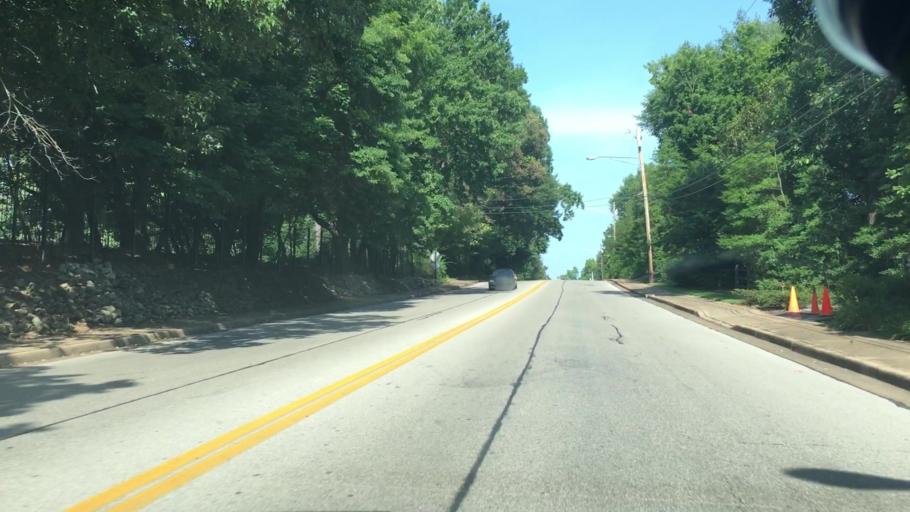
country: US
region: Indiana
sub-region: Vanderburgh County
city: Melody Hill
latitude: 37.9694
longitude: -87.4823
